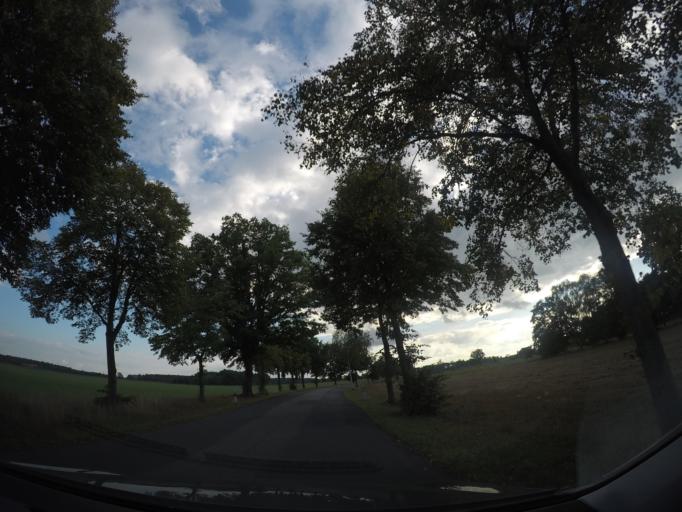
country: DE
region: Saxony-Anhalt
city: Mieste
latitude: 52.5311
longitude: 11.1528
